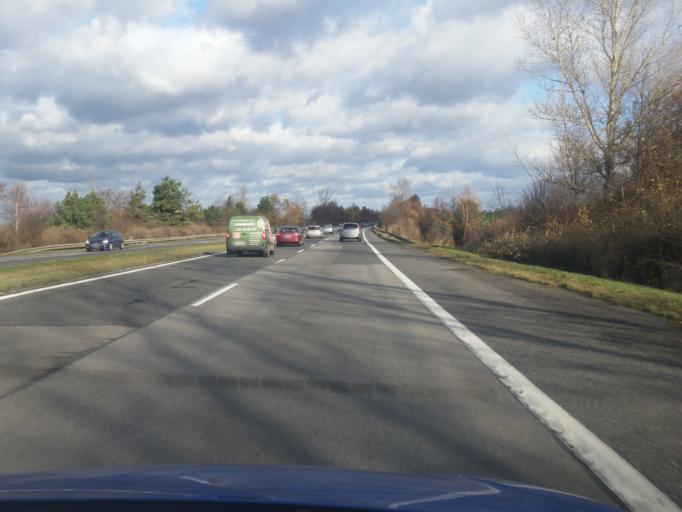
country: PL
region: Silesian Voivodeship
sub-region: Powiat czestochowski
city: Redziny
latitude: 50.8640
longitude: 19.1547
